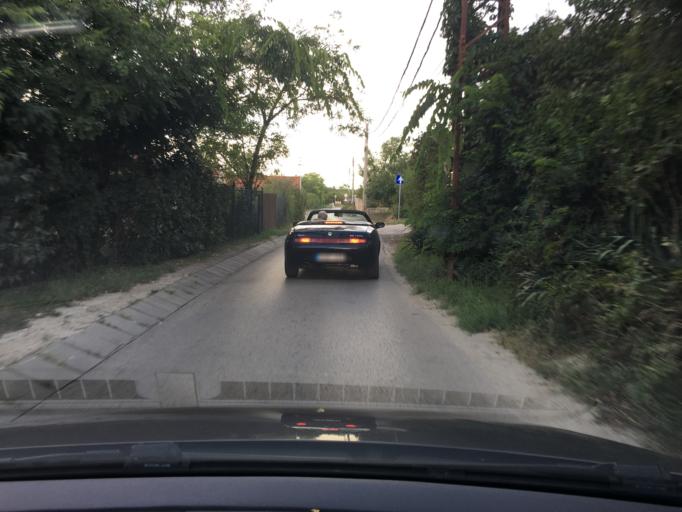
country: HU
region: Pest
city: Szada
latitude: 47.6424
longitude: 19.3079
